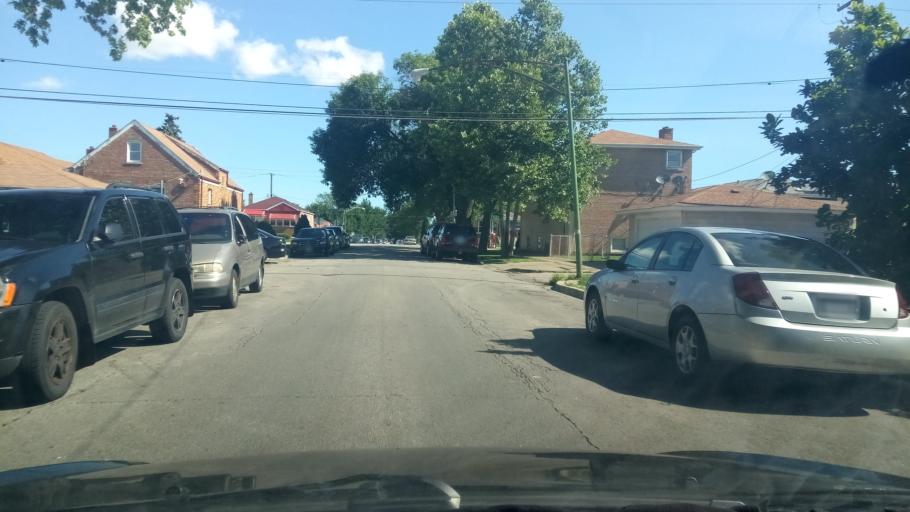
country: US
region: Illinois
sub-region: Cook County
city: Hometown
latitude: 41.7631
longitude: -87.7150
